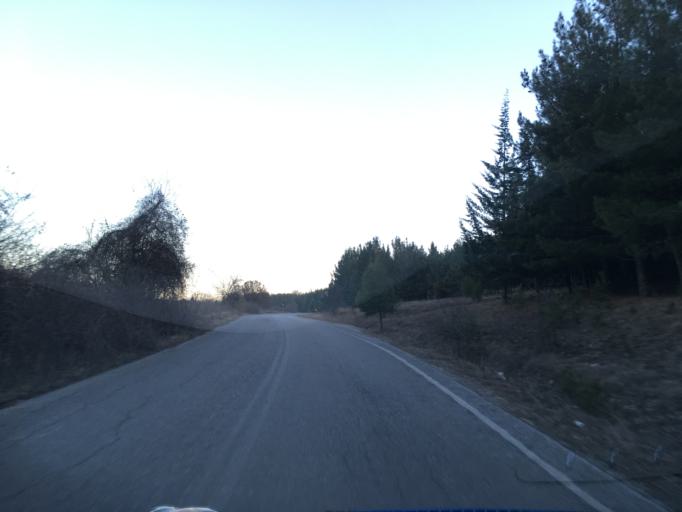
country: GR
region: West Macedonia
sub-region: Nomos Kozanis
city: Koila
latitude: 40.3251
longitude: 21.8133
